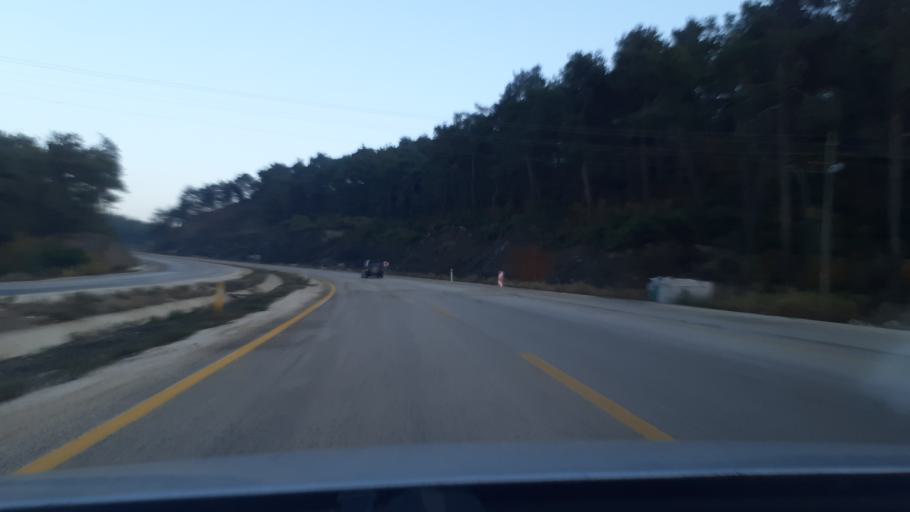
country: TR
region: Hatay
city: Yayladagi
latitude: 35.8911
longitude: 36.0871
